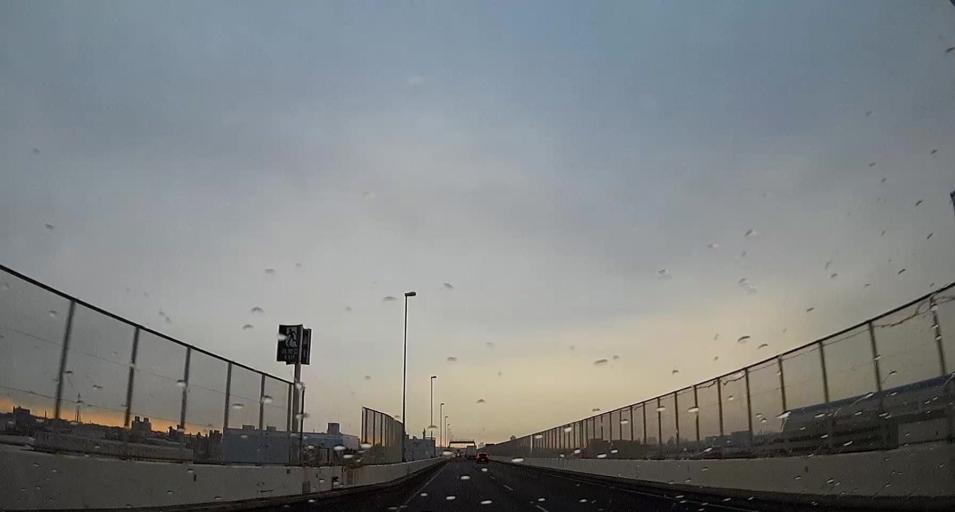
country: JP
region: Kanagawa
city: Yokohama
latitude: 35.4746
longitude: 139.6753
